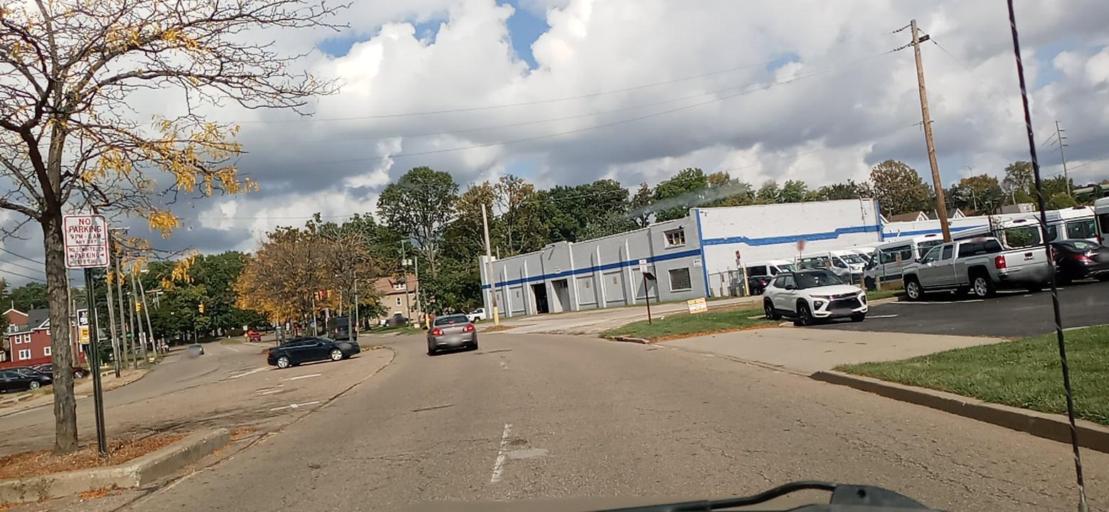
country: US
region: Ohio
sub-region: Summit County
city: Barberton
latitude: 41.0386
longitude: -81.5686
